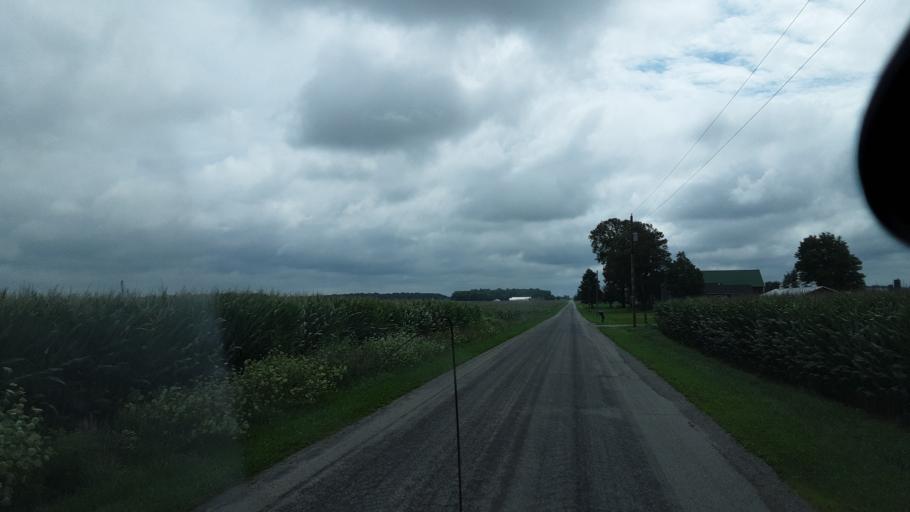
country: US
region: Indiana
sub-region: Wells County
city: Ossian
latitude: 40.8523
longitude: -85.0925
